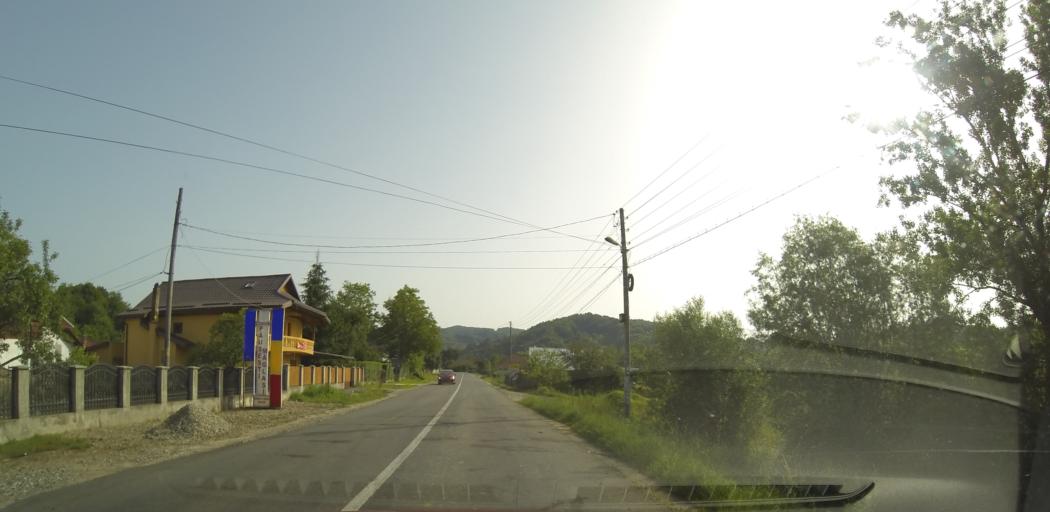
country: RO
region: Valcea
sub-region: Oras Baile Olanesti
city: Olanesti
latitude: 45.1638
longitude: 24.2547
